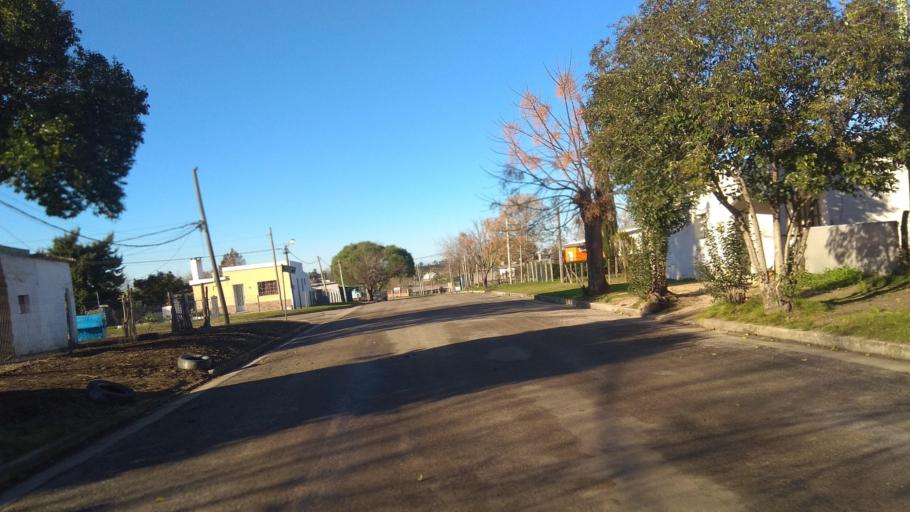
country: UY
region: Florida
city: Florida
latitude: -34.0968
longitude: -56.2389
